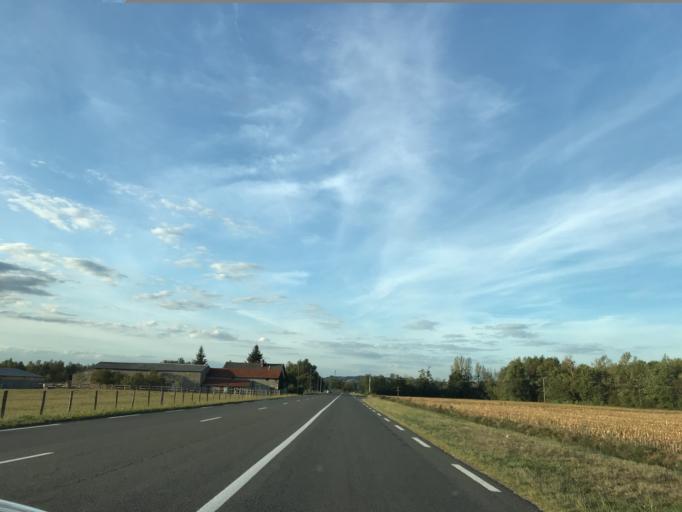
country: FR
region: Auvergne
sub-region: Departement de l'Allier
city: Saint-Yorre
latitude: 46.0355
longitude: 3.4759
